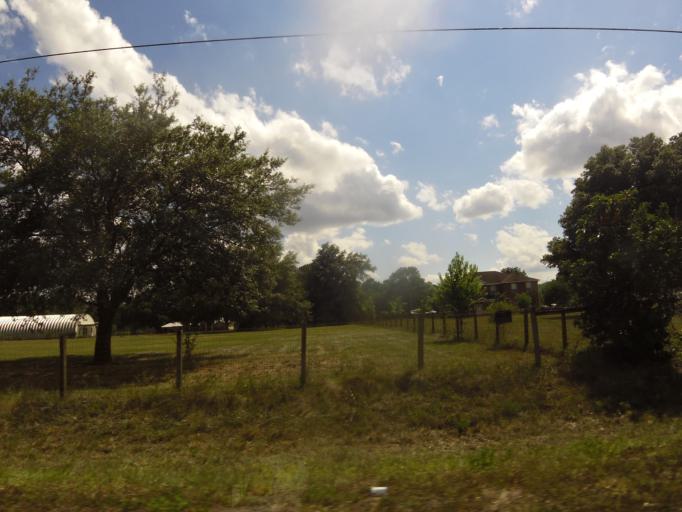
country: US
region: Florida
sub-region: Clay County
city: Keystone Heights
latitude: 29.8702
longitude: -81.9224
